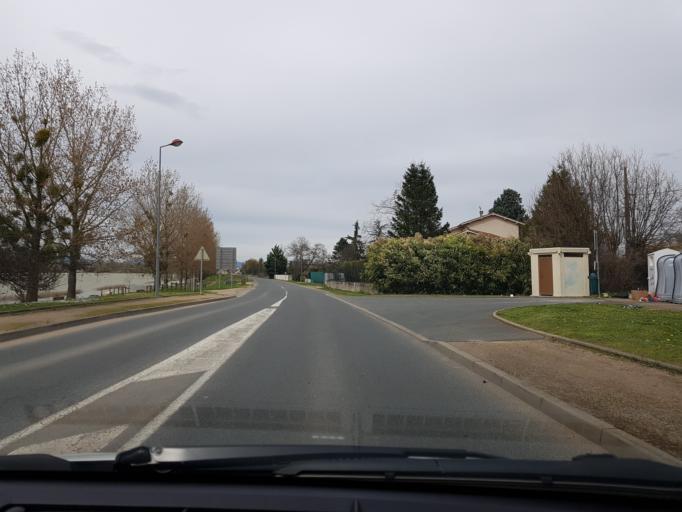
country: FR
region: Rhone-Alpes
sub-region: Departement de l'Ain
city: Jassans-Riottier
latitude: 45.9761
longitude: 4.7564
